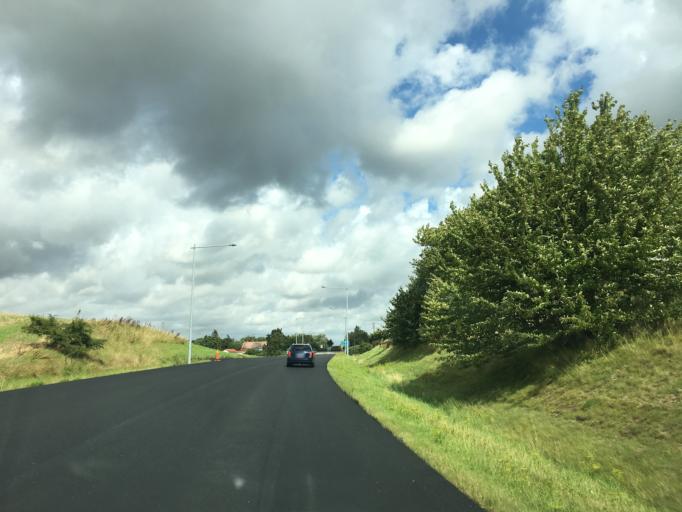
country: SE
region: Skane
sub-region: Svedala Kommun
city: Svedala
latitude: 55.5158
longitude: 13.2061
